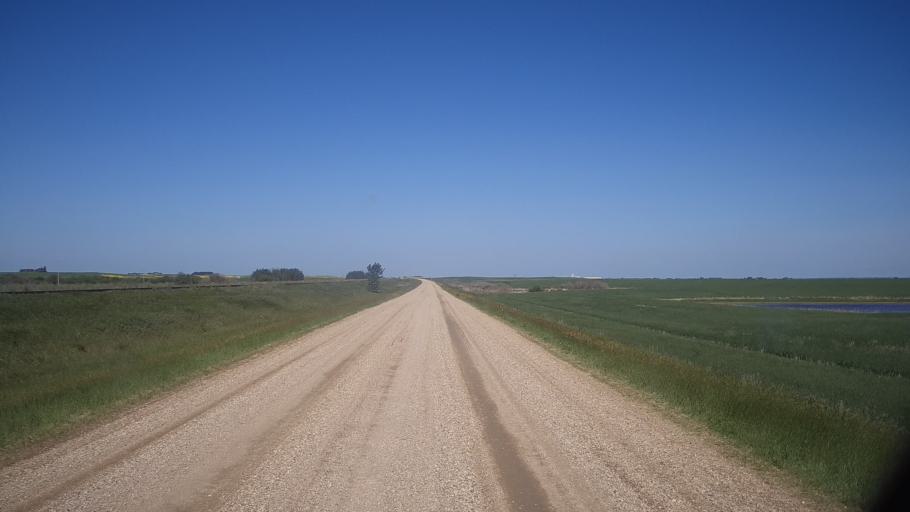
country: CA
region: Saskatchewan
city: Watrous
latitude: 51.8428
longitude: -105.9132
